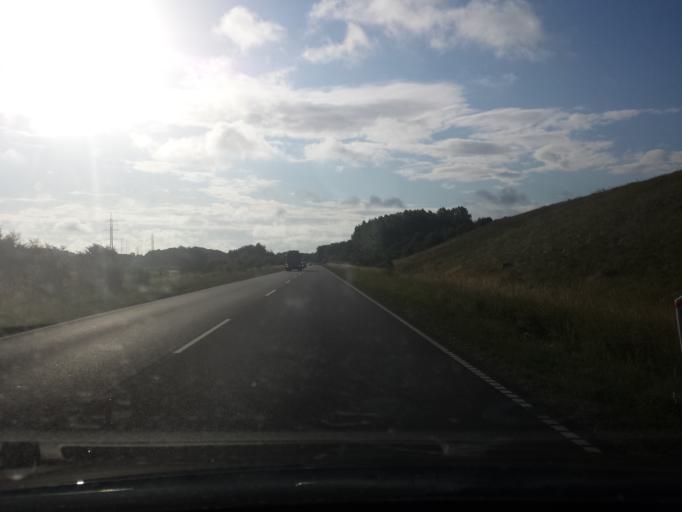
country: DK
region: South Denmark
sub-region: Sonderborg Kommune
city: Sonderborg
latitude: 54.9313
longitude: 9.8309
